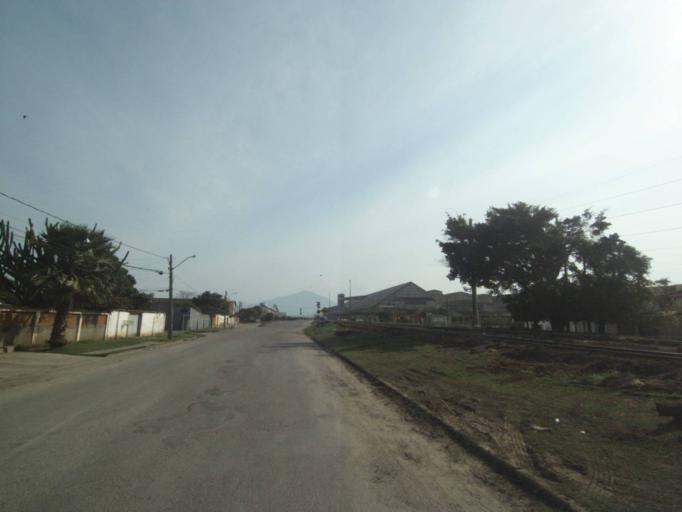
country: BR
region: Parana
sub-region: Paranagua
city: Paranagua
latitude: -25.5363
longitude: -48.5344
